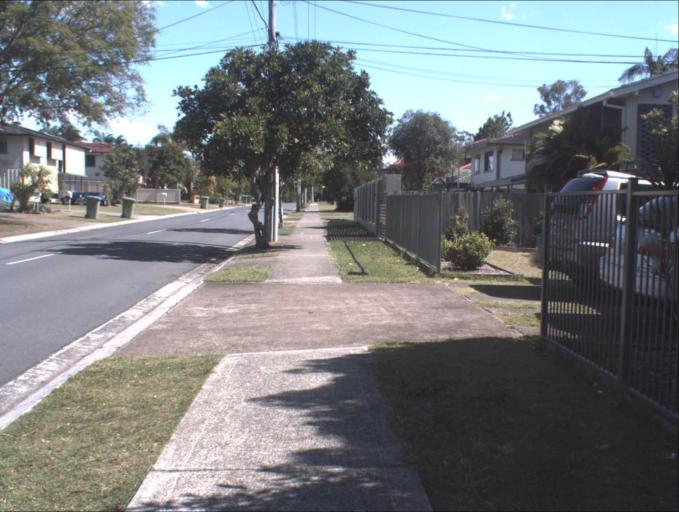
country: AU
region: Queensland
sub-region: Logan
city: Rochedale South
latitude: -27.5961
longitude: 153.1160
